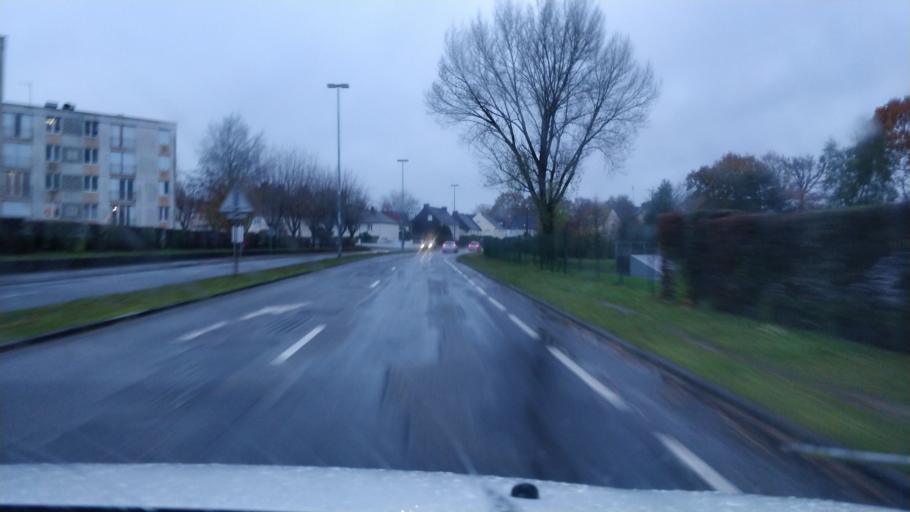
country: FR
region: Brittany
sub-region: Departement des Cotes-d'Armor
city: Loudeac
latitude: 48.1789
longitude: -2.7493
